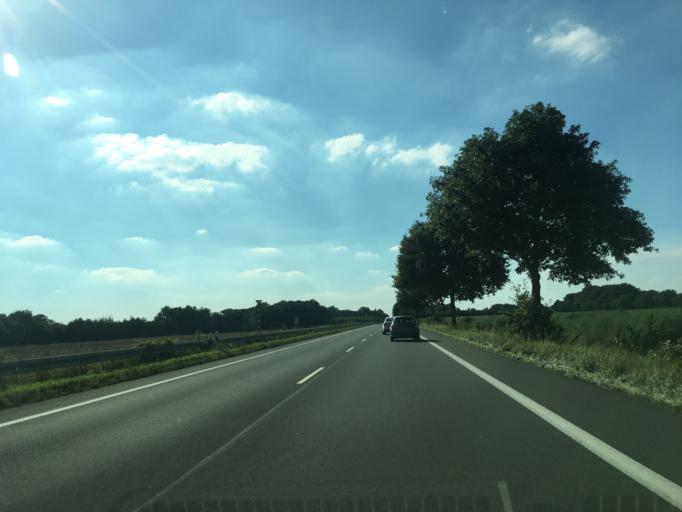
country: DE
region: North Rhine-Westphalia
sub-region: Regierungsbezirk Munster
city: Sassenberg
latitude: 51.9448
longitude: 8.0486
